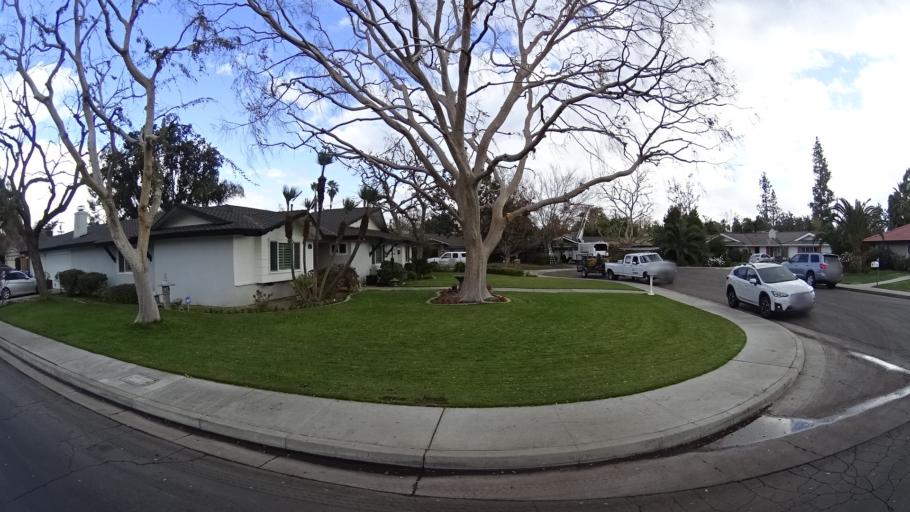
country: US
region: California
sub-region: Kern County
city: Greenacres
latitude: 35.3521
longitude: -119.0838
